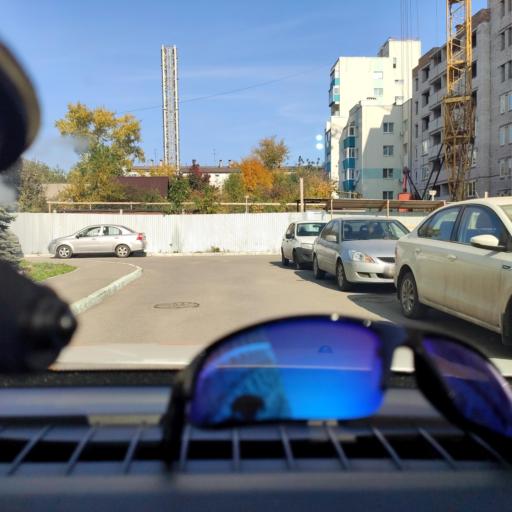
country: RU
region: Samara
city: Samara
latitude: 53.1979
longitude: 50.1840
